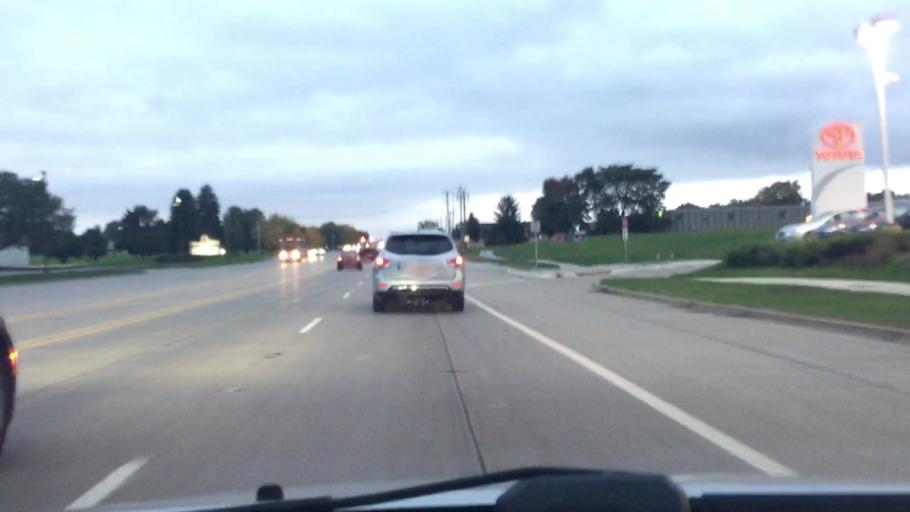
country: US
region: Illinois
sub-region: McHenry County
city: Crystal Lake
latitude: 42.2127
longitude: -88.2864
